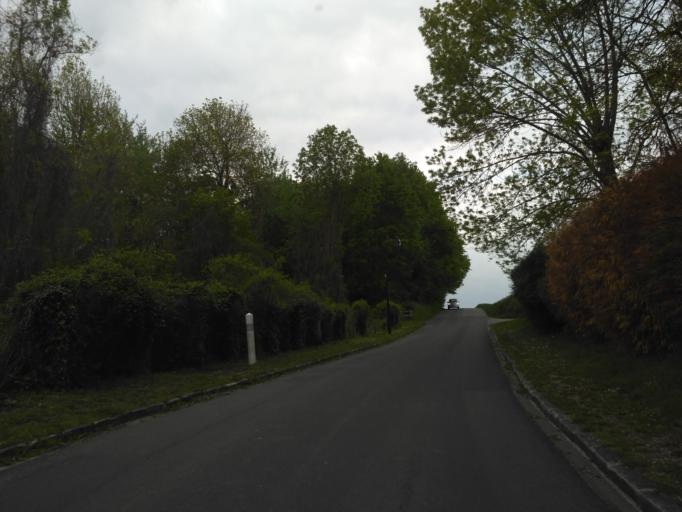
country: FR
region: Ile-de-France
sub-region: Departement de Seine-et-Marne
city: Moisenay
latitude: 48.5734
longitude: 2.7822
